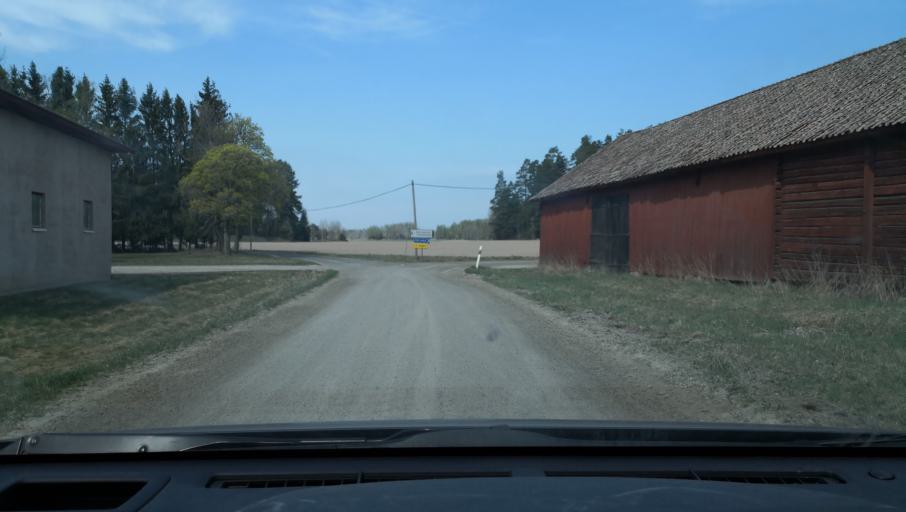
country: SE
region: Vaestmanland
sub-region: Vasteras
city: Skultuna
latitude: 59.7859
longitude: 16.4578
